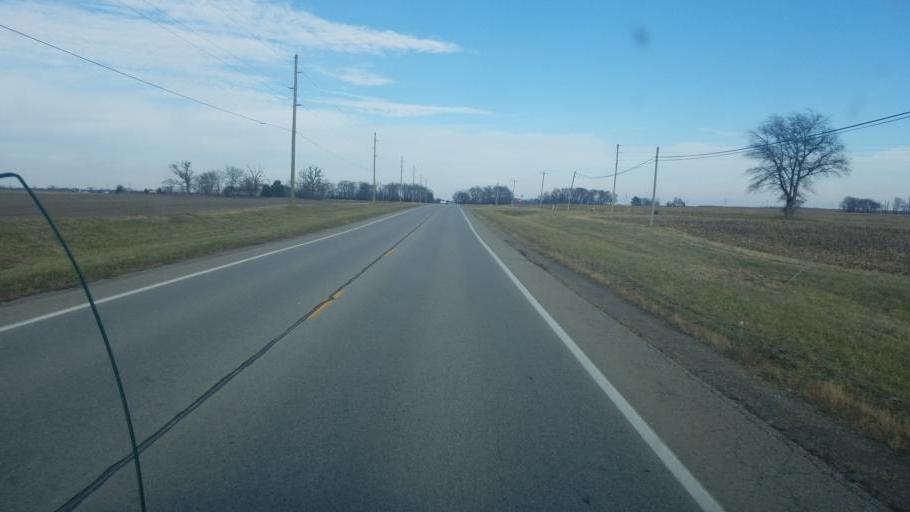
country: US
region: Illinois
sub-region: White County
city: Carmi
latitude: 38.1148
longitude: -88.1169
